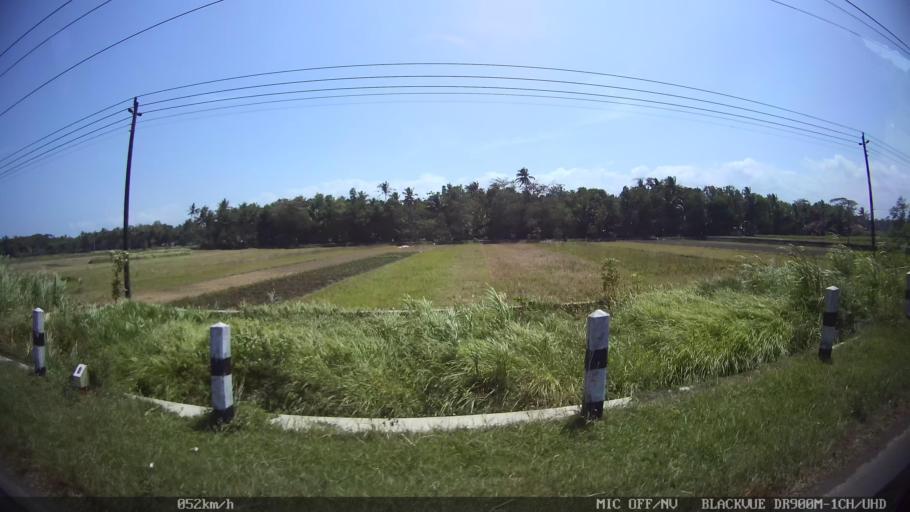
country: ID
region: Daerah Istimewa Yogyakarta
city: Srandakan
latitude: -7.9515
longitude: 110.2081
